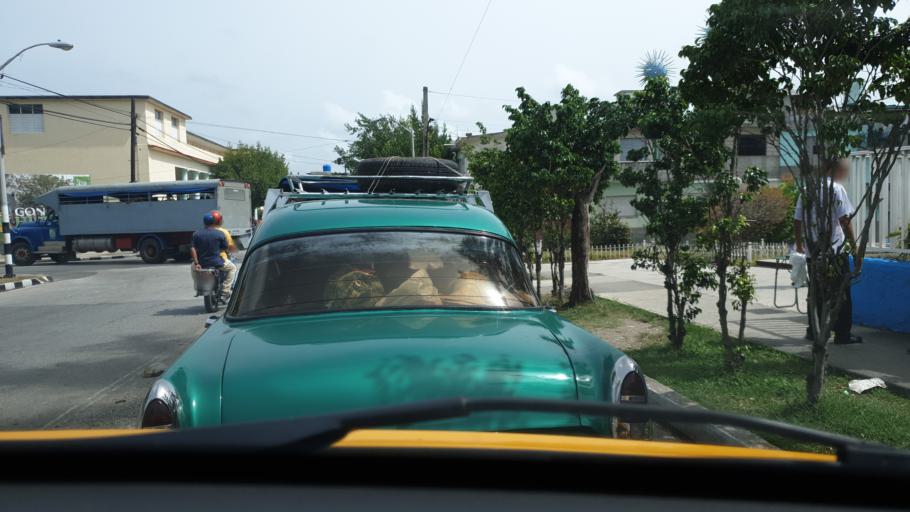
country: CU
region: Villa Clara
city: Santa Clara
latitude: 22.3998
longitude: -79.9639
